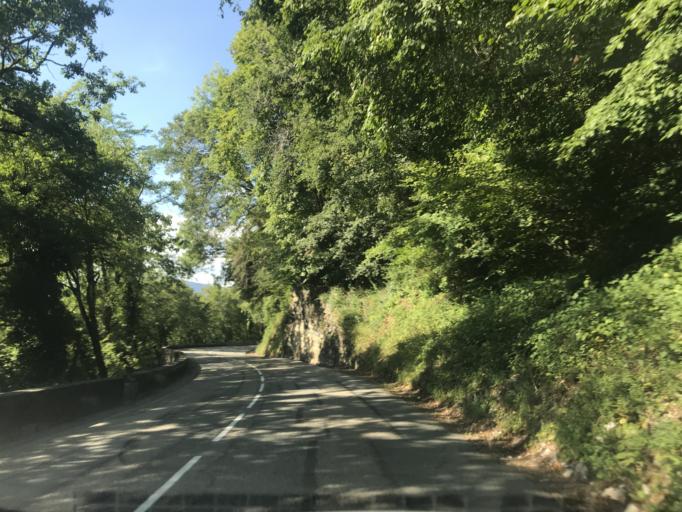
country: FR
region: Rhone-Alpes
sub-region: Departement de la Savoie
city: Chatillon
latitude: 45.7862
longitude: 5.7844
